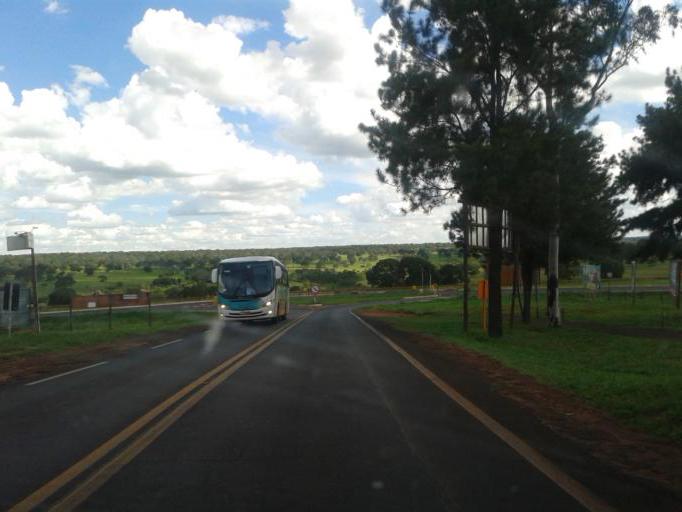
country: BR
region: Minas Gerais
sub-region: Santa Vitoria
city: Santa Vitoria
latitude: -18.8748
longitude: -50.1224
